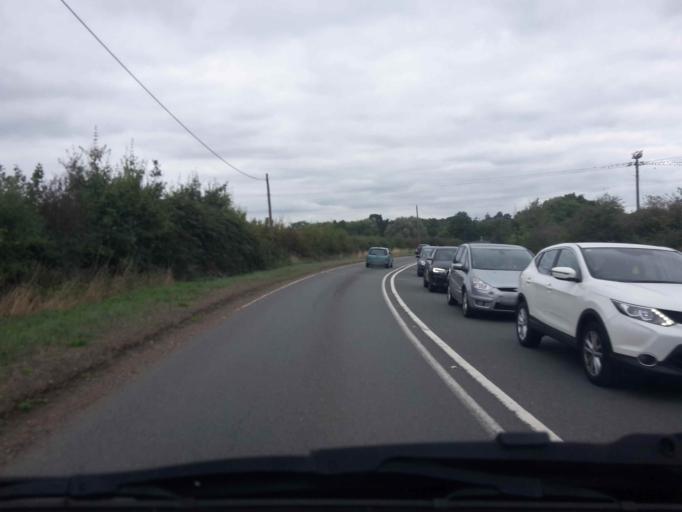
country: GB
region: England
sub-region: Hampshire
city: Eversley
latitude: 51.3436
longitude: -0.8820
